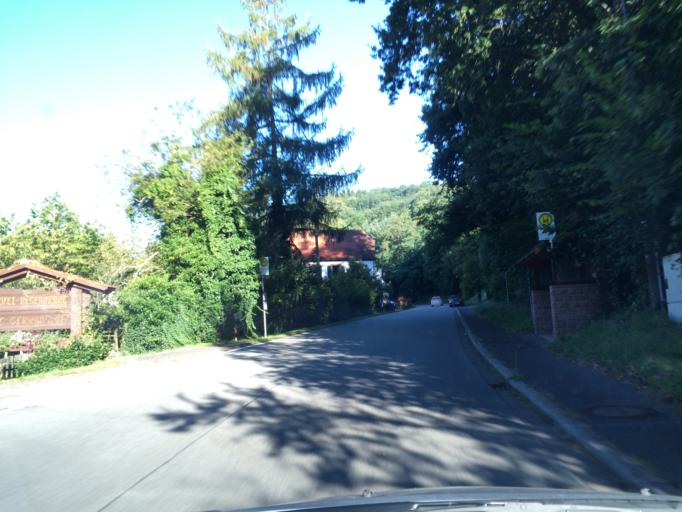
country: DE
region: Rheinland-Pfalz
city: Bobenthal
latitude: 49.0469
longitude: 7.9006
